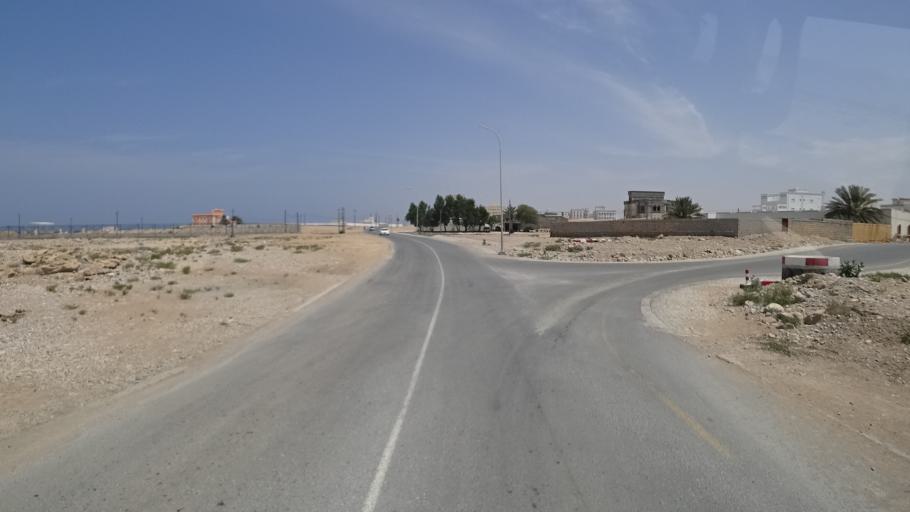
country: OM
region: Ash Sharqiyah
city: Sur
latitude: 22.6102
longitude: 59.4685
